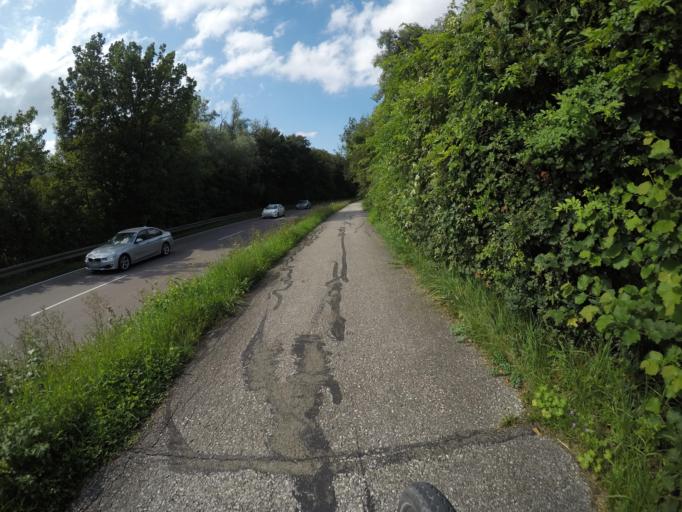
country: DE
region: Baden-Wuerttemberg
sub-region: Regierungsbezirk Stuttgart
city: Unterensingen
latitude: 48.6540
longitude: 9.3612
